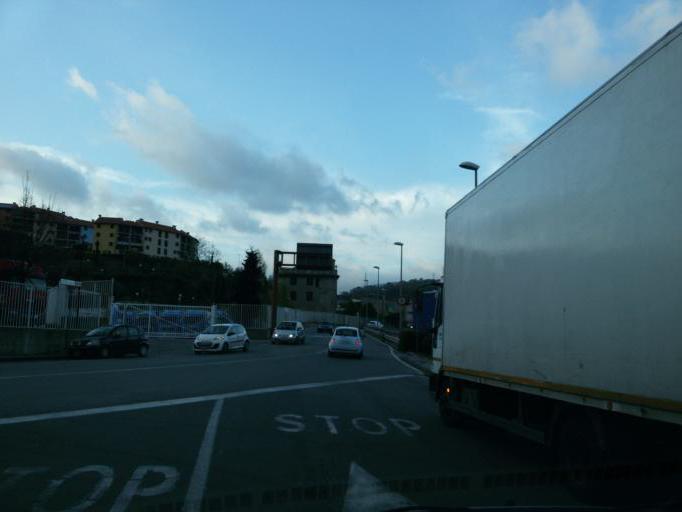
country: IT
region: Liguria
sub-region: Provincia di Genova
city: Manesseno
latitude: 44.4690
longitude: 8.8993
